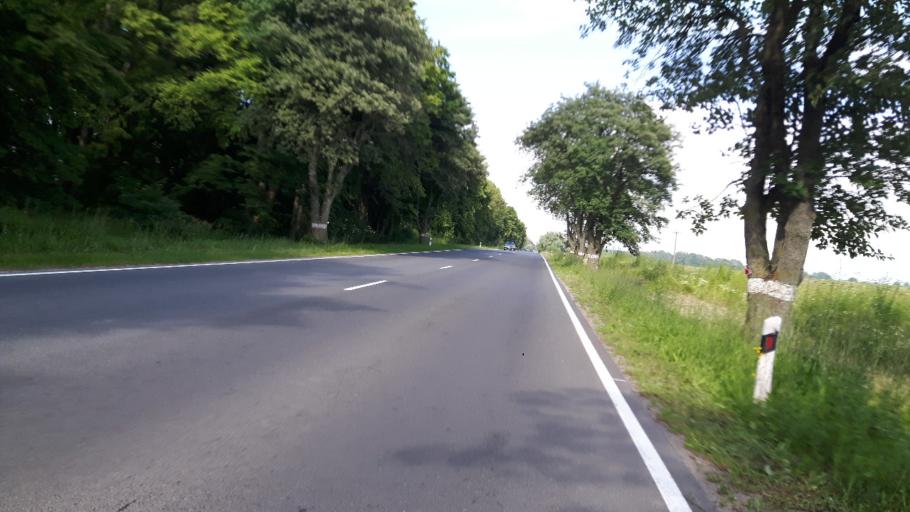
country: RU
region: Kaliningrad
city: Mamonovo
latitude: 54.4675
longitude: 19.9675
